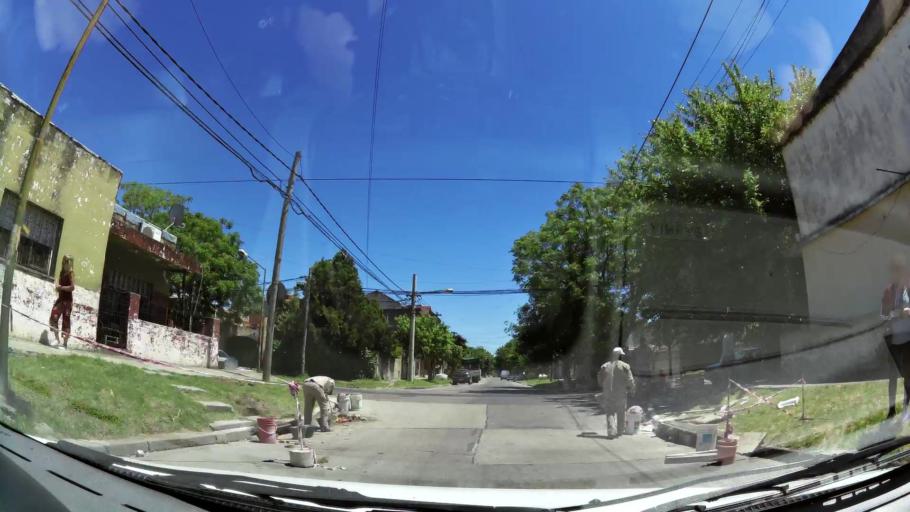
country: AR
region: Buenos Aires
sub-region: Partido de San Isidro
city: San Isidro
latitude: -34.5106
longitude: -58.5530
